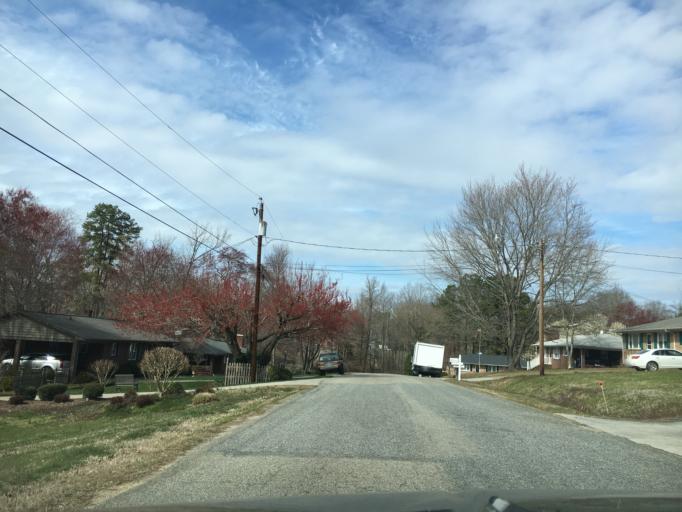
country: US
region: Virginia
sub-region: Halifax County
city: South Boston
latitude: 36.7292
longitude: -78.9176
